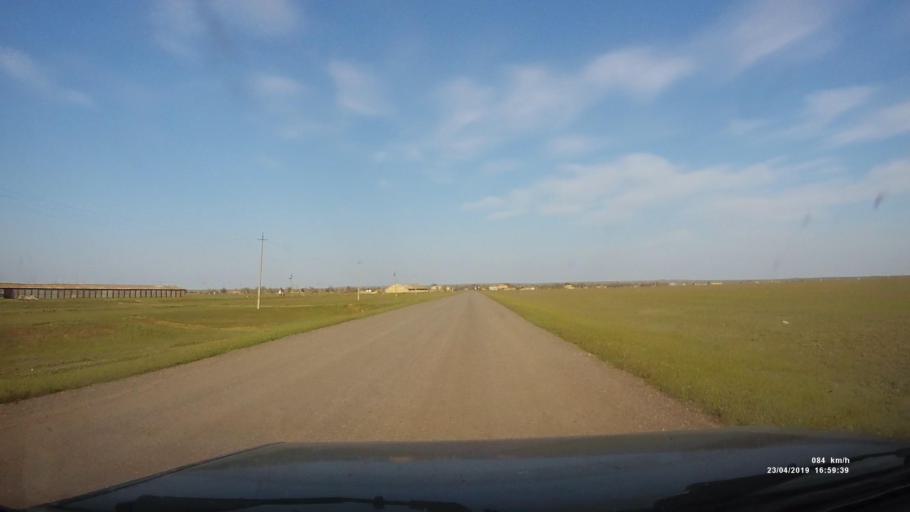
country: RU
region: Kalmykiya
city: Priyutnoye
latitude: 46.3085
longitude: 43.3931
